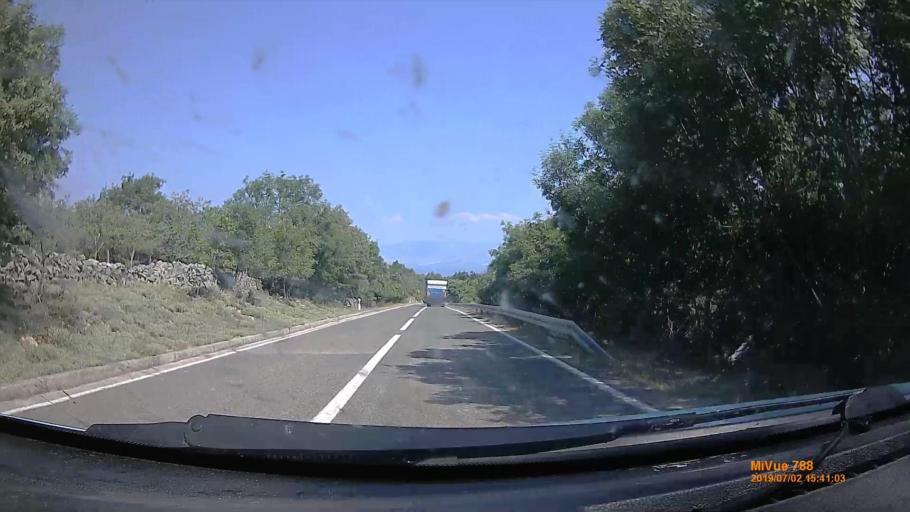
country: HR
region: Primorsko-Goranska
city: Cres
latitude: 44.9615
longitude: 14.4372
